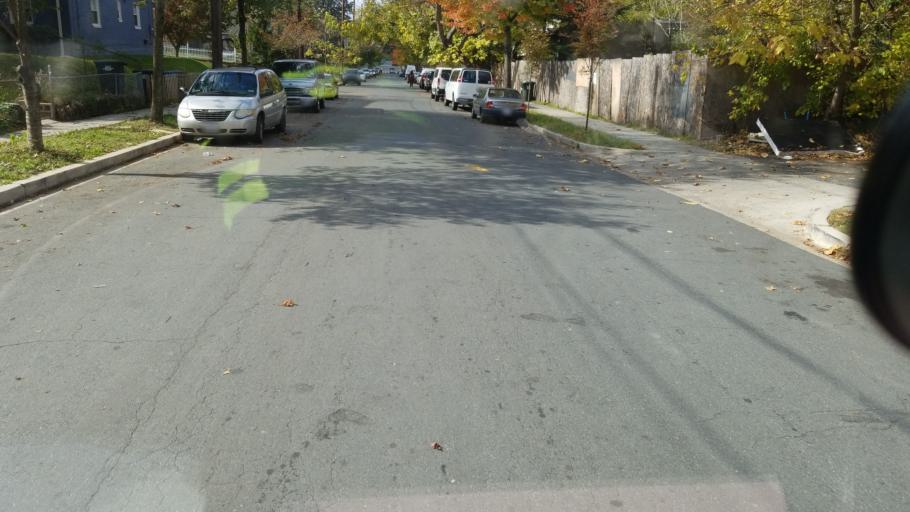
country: US
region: Maryland
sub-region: Prince George's County
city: Fairmount Heights
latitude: 38.8971
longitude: -76.9157
